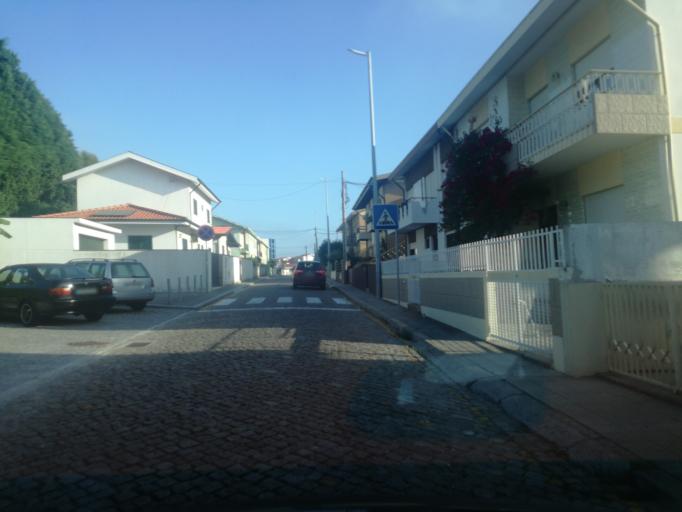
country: PT
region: Porto
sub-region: Maia
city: Gemunde
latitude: 41.2484
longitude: -8.6586
